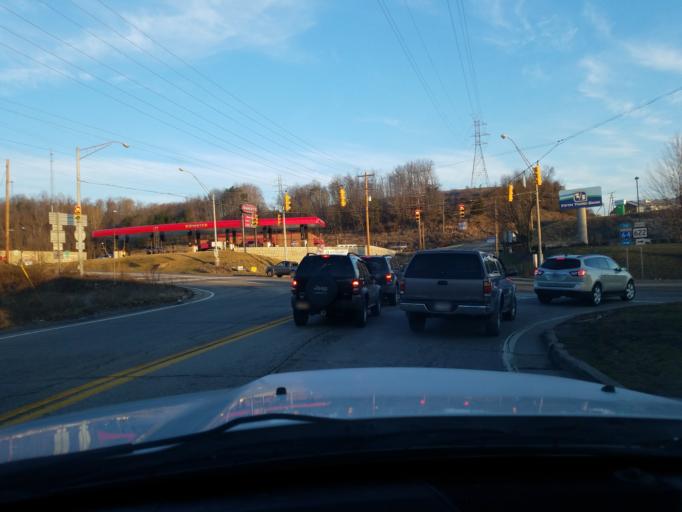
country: US
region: West Virginia
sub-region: Kanawha County
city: Cross Lanes
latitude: 38.4120
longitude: -81.7985
